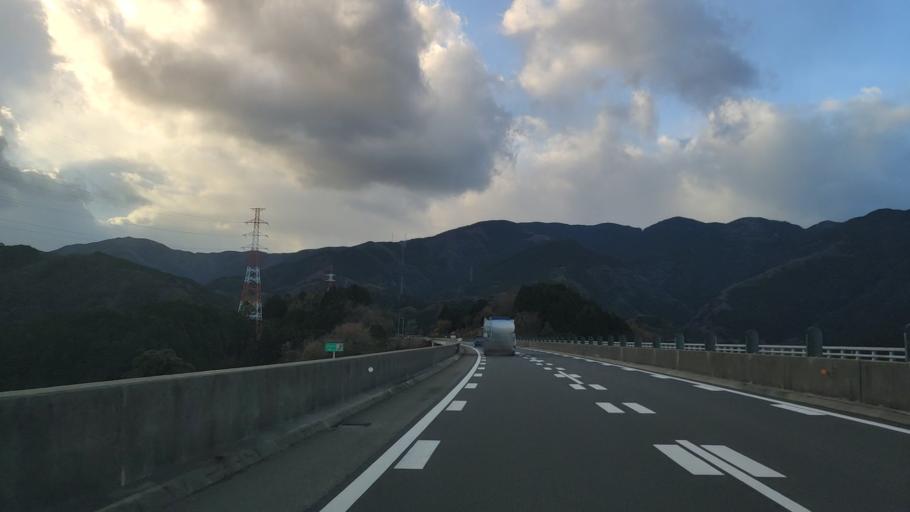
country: JP
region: Ehime
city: Saijo
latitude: 33.8539
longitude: 133.0095
